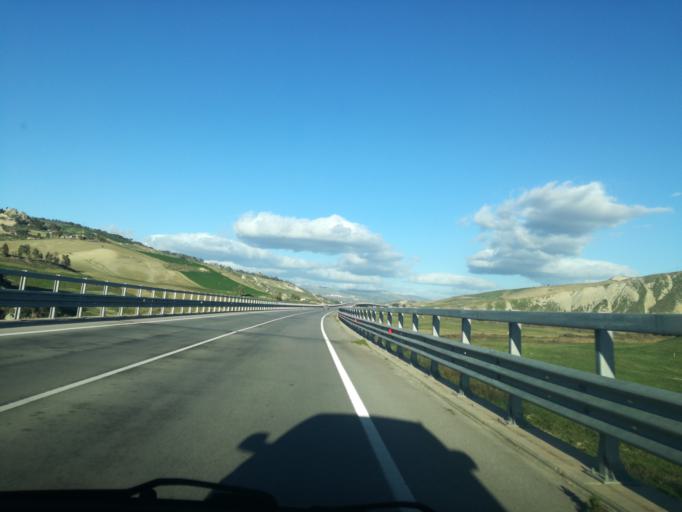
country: IT
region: Sicily
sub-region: Enna
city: Pietraperzia
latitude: 37.4257
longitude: 14.0755
